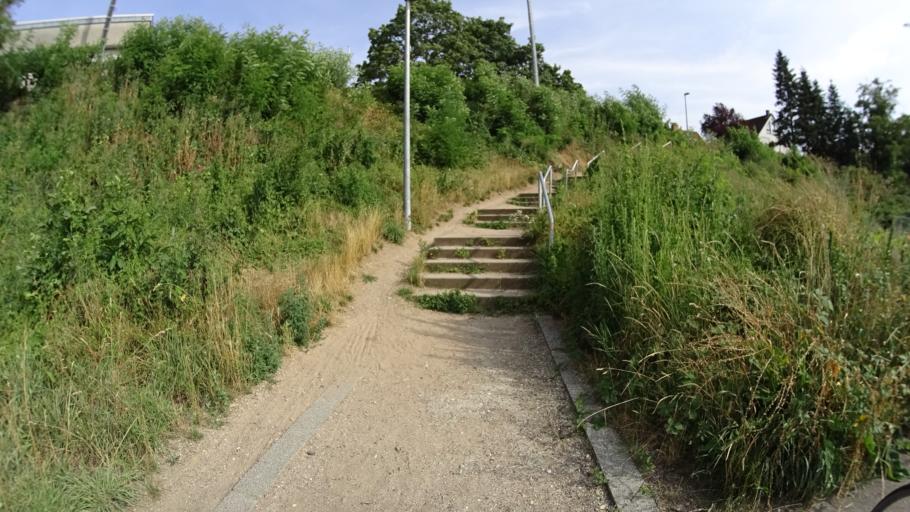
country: DE
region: Baden-Wuerttemberg
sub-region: Karlsruhe Region
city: Karlsruhe
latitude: 49.0375
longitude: 8.3411
